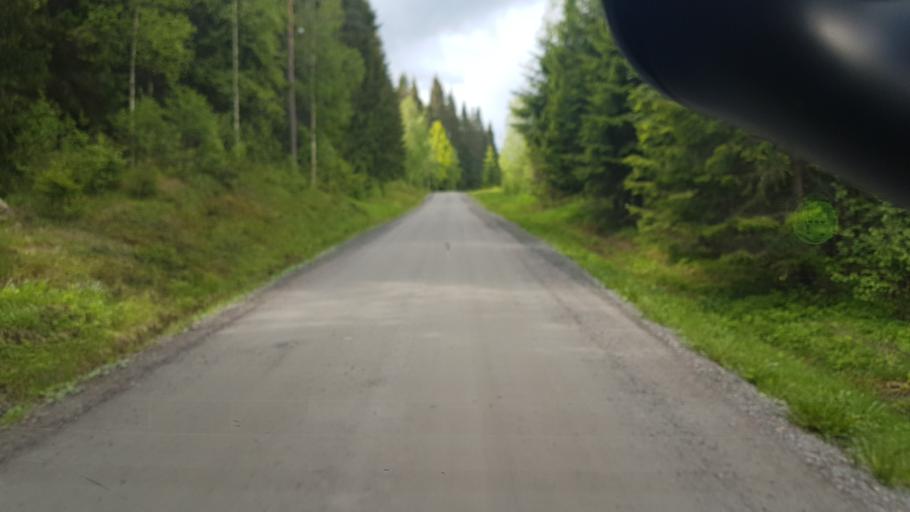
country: NO
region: Ostfold
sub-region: Romskog
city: Romskog
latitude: 59.6909
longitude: 11.9408
